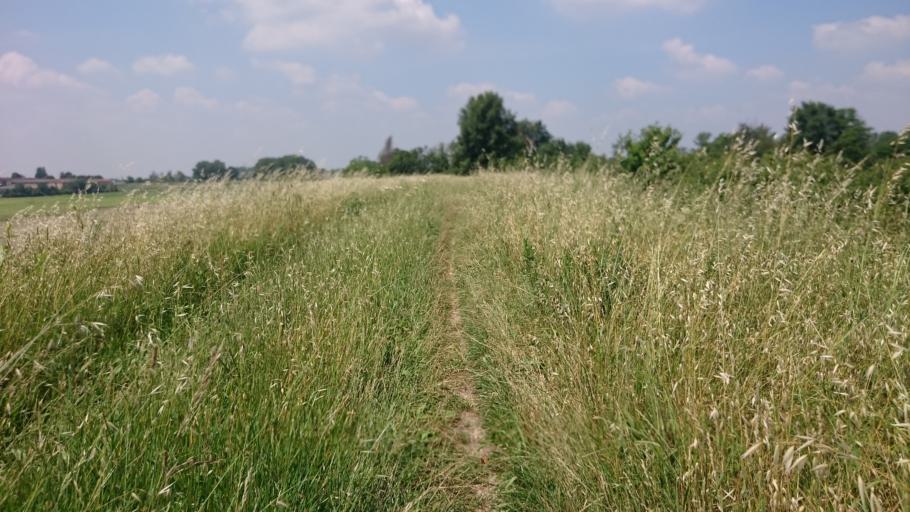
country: IT
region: Lombardy
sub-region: Provincia di Mantova
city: San Biagio
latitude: 45.1256
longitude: 10.8440
